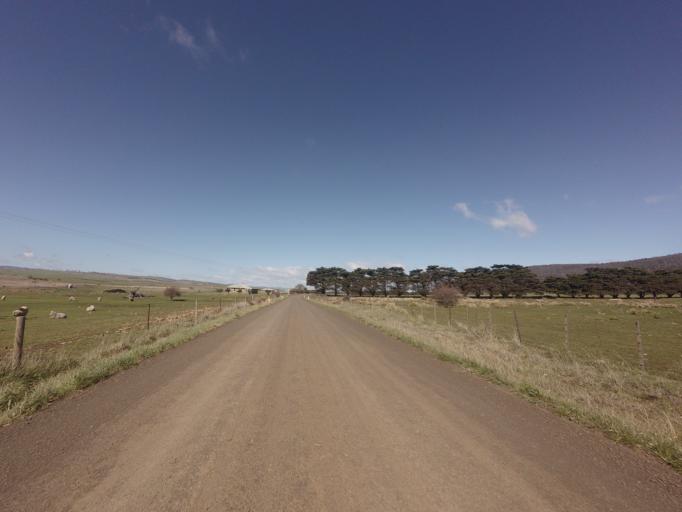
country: AU
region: Tasmania
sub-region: Northern Midlands
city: Evandale
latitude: -41.9492
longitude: 147.4341
